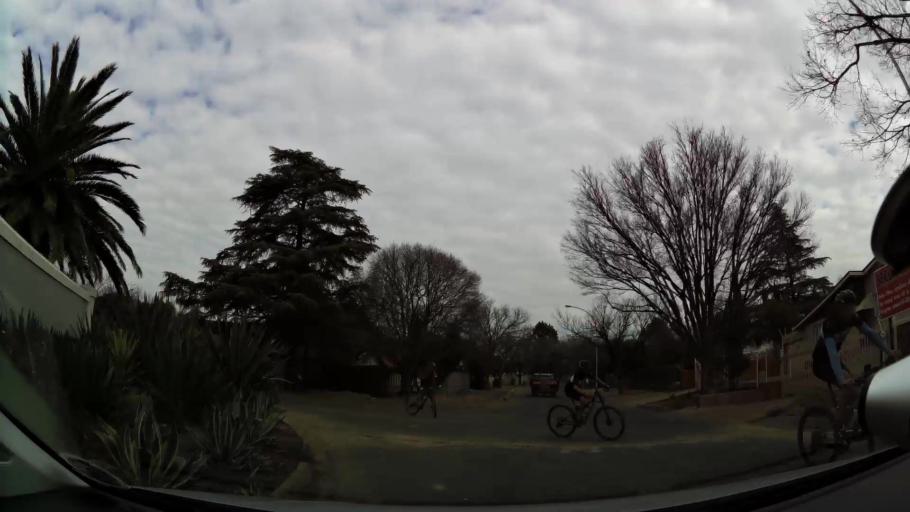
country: ZA
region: Orange Free State
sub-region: Mangaung Metropolitan Municipality
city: Bloemfontein
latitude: -29.0952
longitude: 26.2127
